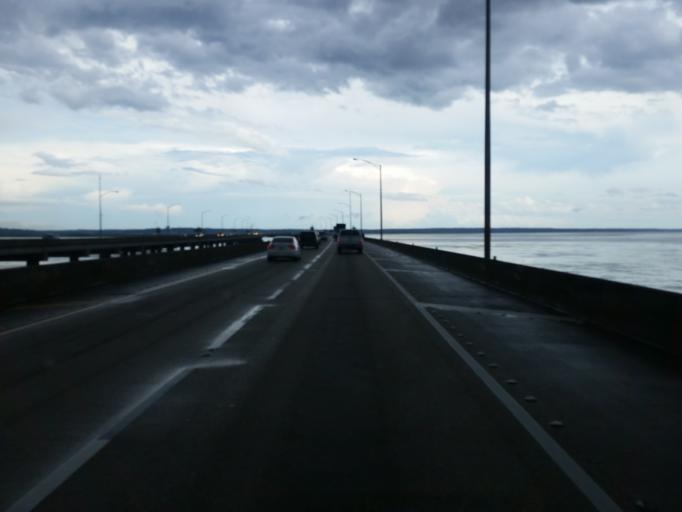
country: US
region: Alabama
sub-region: Baldwin County
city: Spanish Fort
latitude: 30.6728
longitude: -87.9802
